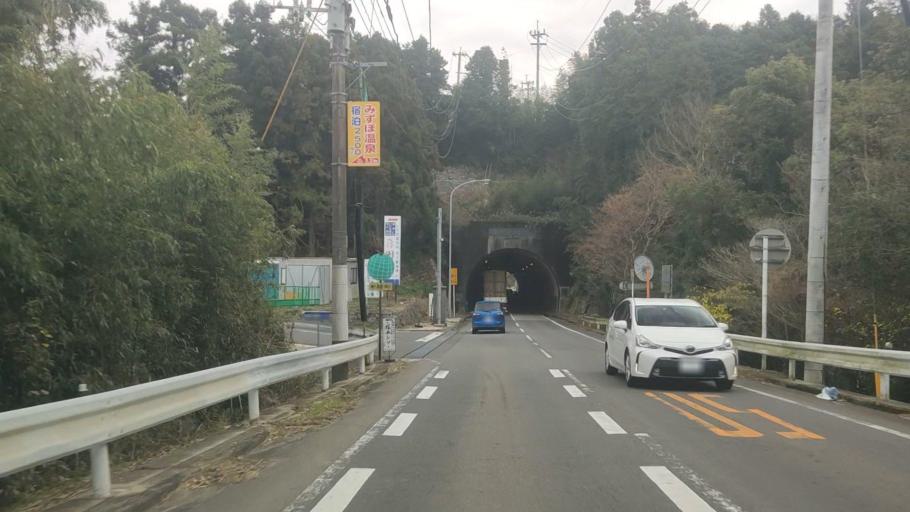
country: JP
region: Nagasaki
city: Shimabara
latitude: 32.8490
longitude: 130.2301
